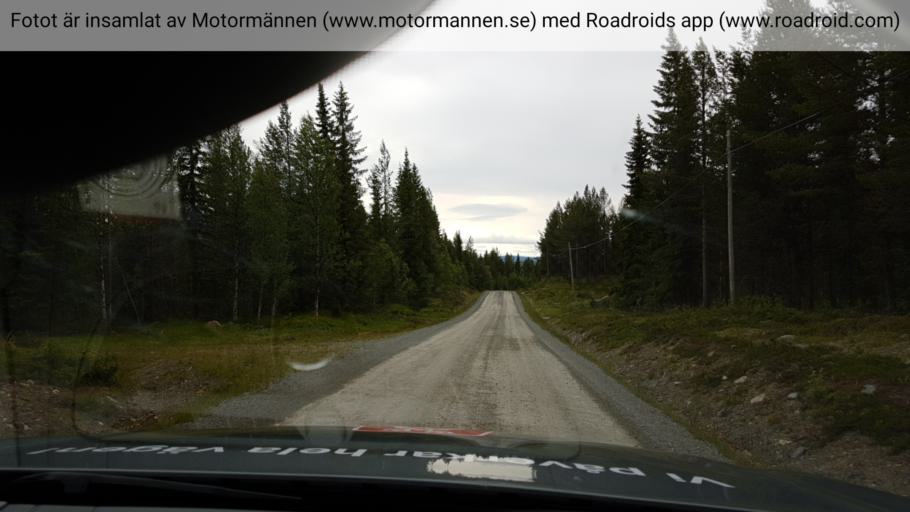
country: SE
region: Jaemtland
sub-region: Are Kommun
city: Jarpen
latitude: 62.8295
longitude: 13.8212
